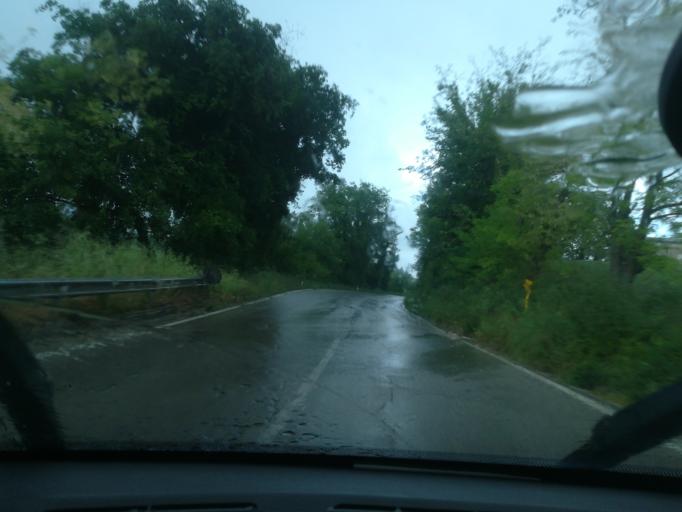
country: IT
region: The Marches
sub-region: Provincia di Macerata
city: Sforzacosta
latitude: 43.2882
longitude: 13.4093
